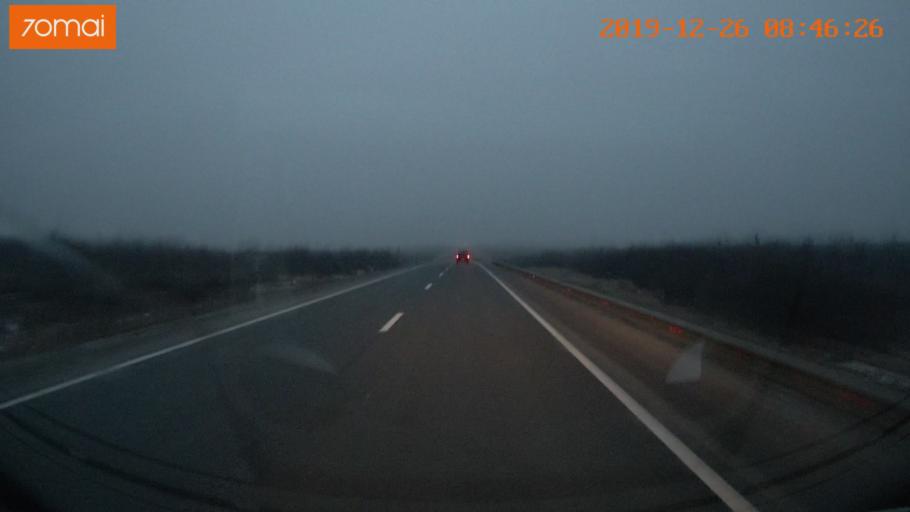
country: RU
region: Jaroslavl
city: Prechistoye
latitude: 58.6113
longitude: 40.3369
